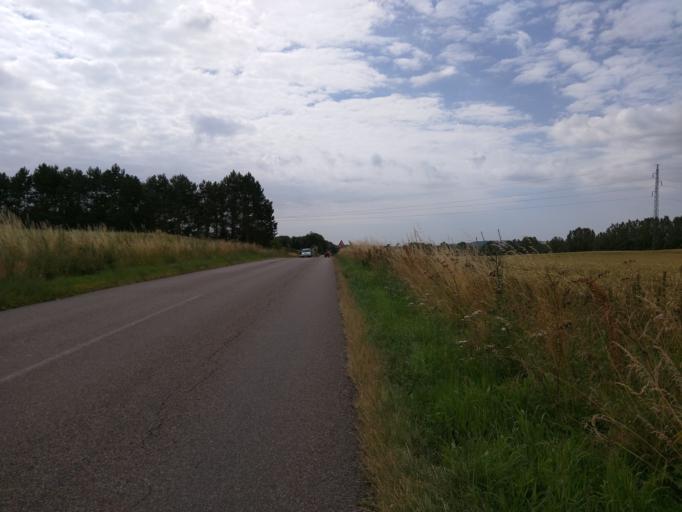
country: DK
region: Zealand
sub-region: Kalundborg Kommune
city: Svebolle
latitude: 55.7040
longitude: 11.3042
